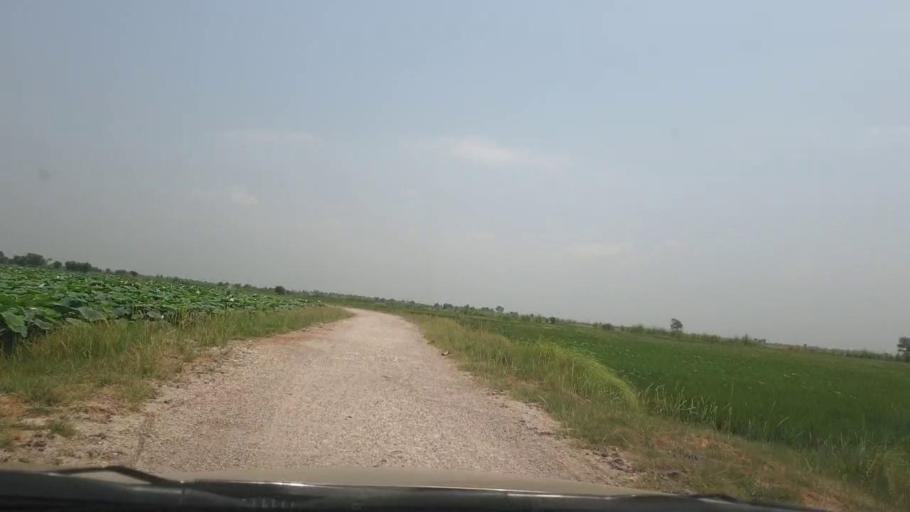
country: PK
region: Sindh
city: Ratodero
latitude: 27.7345
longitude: 68.3134
